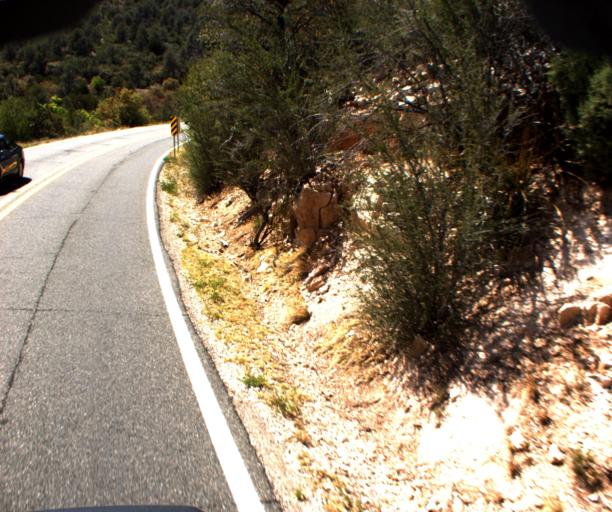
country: US
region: Arizona
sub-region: Yavapai County
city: Clarkdale
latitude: 34.7413
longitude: -112.1375
